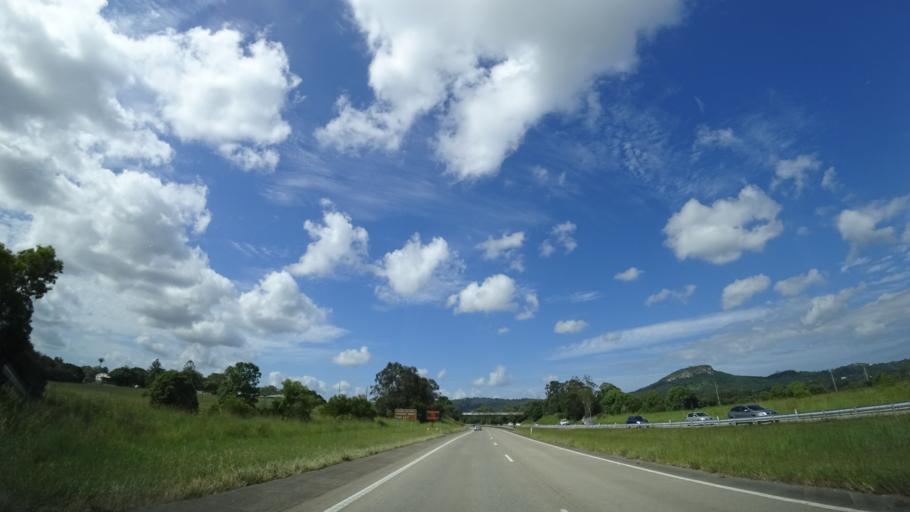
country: AU
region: Queensland
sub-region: Sunshine Coast
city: Yandina
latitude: -26.5668
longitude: 152.9650
